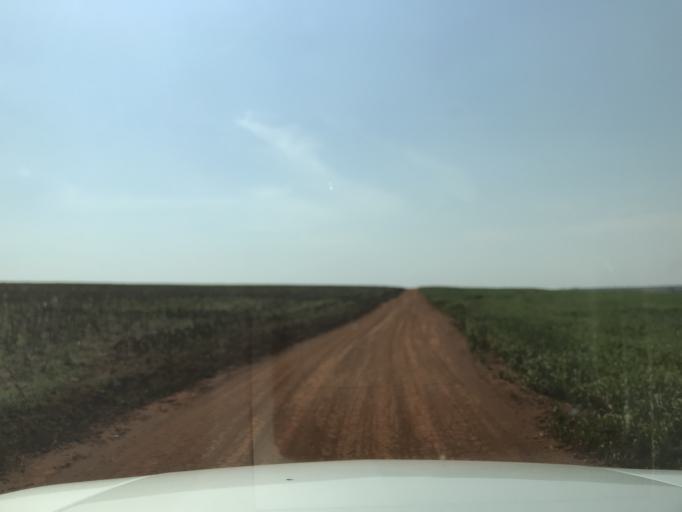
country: BR
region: Parana
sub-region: Palotina
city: Palotina
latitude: -24.2305
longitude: -53.7441
